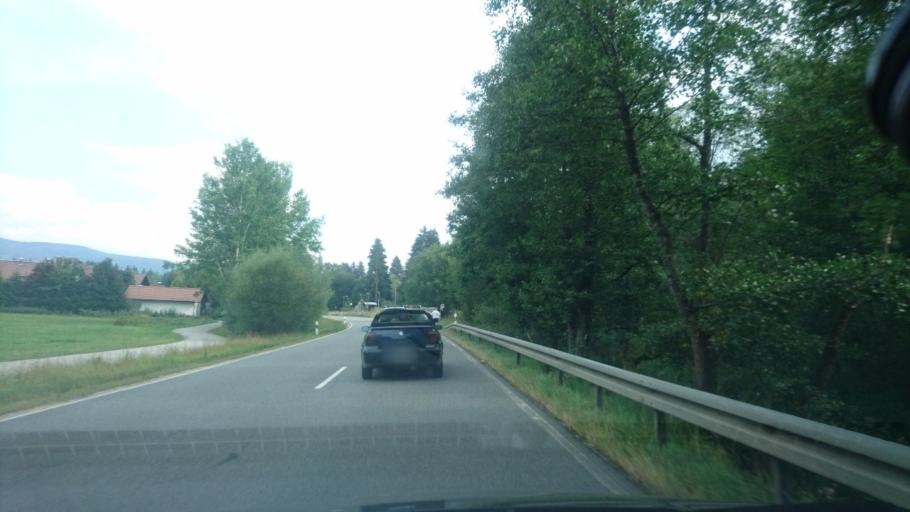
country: DE
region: Bavaria
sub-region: Lower Bavaria
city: Frauenau
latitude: 49.0079
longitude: 13.2757
